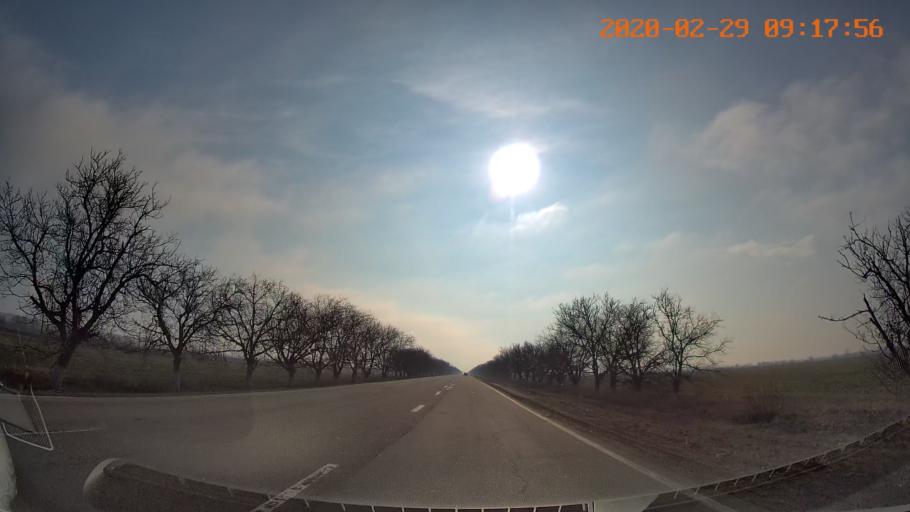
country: MD
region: Telenesti
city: Pervomaisc
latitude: 46.7783
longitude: 29.9136
